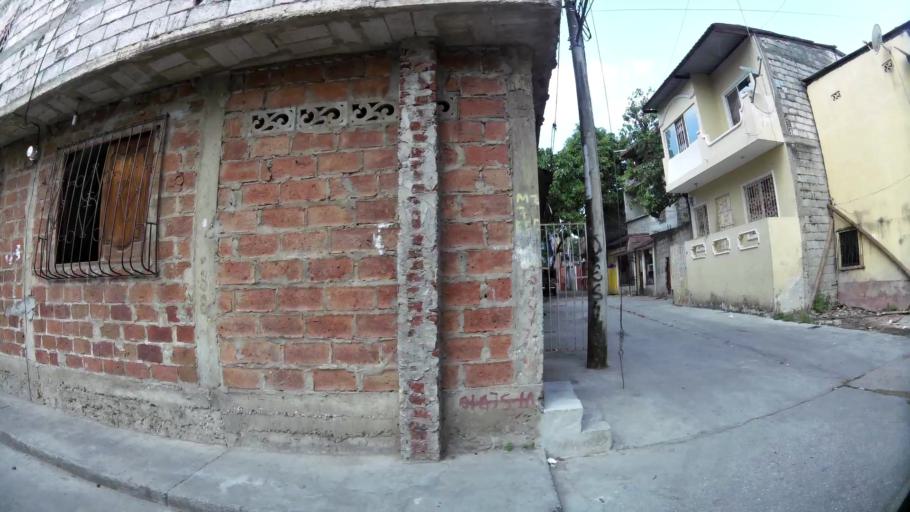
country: EC
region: Guayas
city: Guayaquil
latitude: -2.1404
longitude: -79.9362
